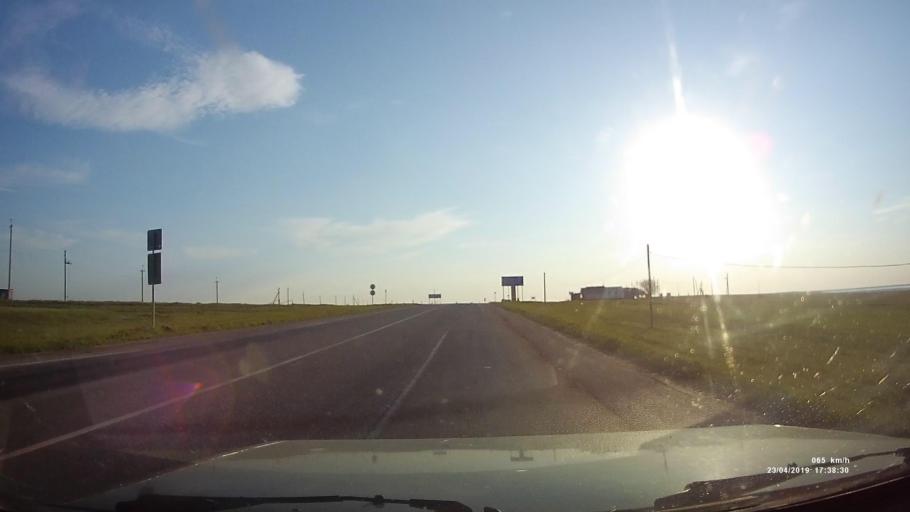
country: RU
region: Kalmykiya
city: Priyutnoye
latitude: 46.0915
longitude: 43.4895
